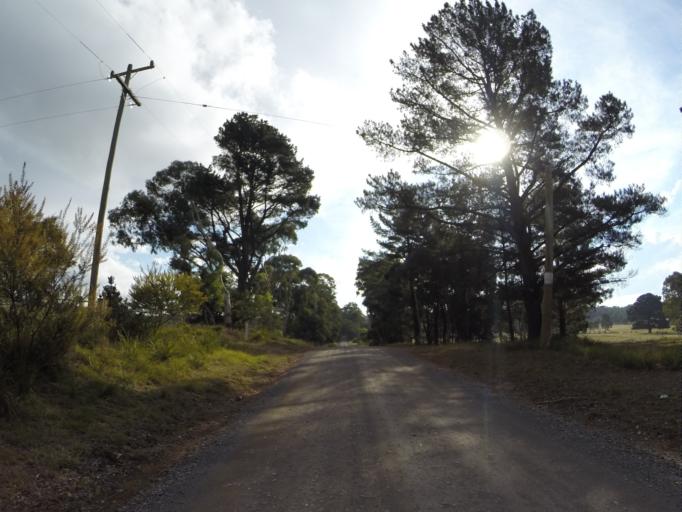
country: AU
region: New South Wales
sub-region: Wingecarribee
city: Bundanoon
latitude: -34.5330
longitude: 150.2211
